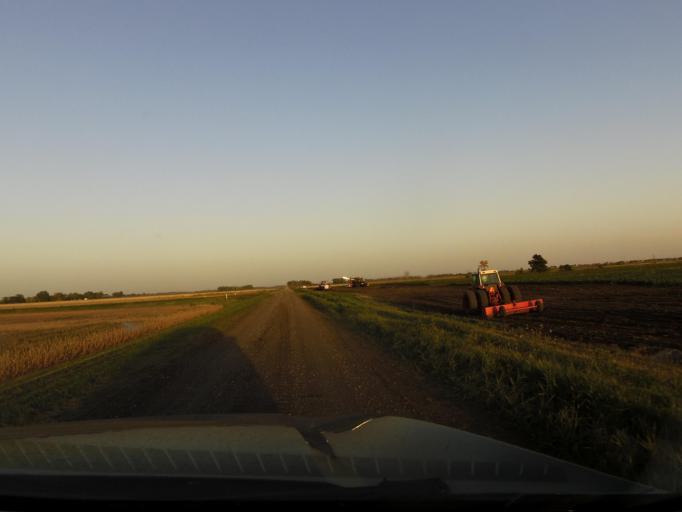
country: US
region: North Dakota
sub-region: Walsh County
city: Grafton
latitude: 48.3832
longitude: -97.2255
